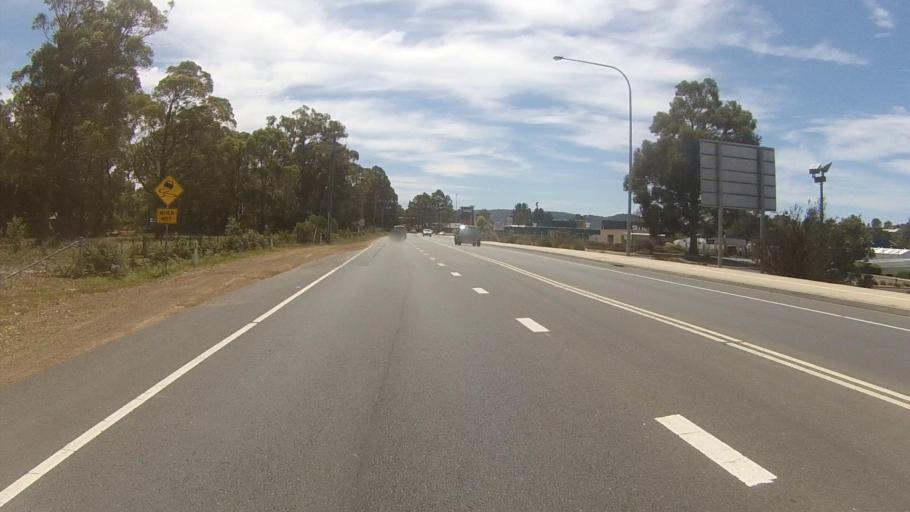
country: AU
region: Tasmania
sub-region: Kingborough
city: Kingston
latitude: -42.9862
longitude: 147.2905
